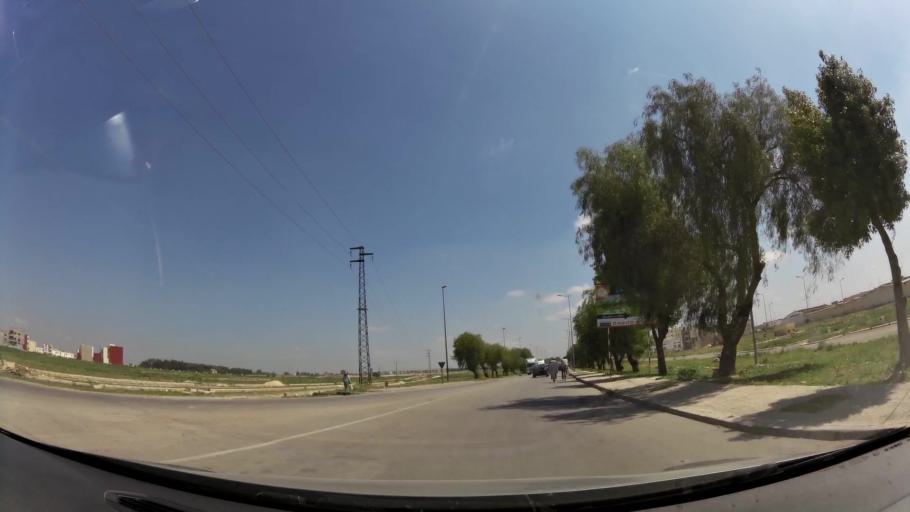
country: MA
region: Fes-Boulemane
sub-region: Fes
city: Fes
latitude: 34.0084
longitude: -5.0461
